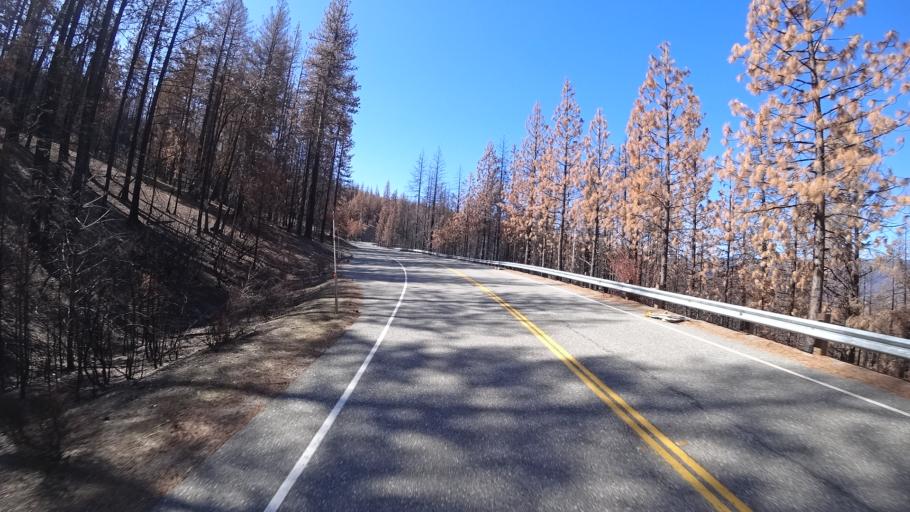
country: US
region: California
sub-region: Tehama County
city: Rancho Tehama Reserve
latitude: 39.6667
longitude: -122.7154
